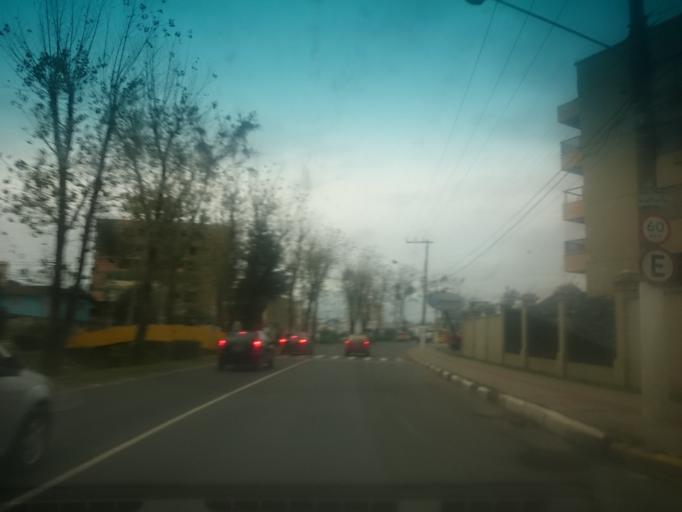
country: BR
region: Santa Catarina
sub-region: Lages
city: Lages
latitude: -27.8077
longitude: -50.3230
